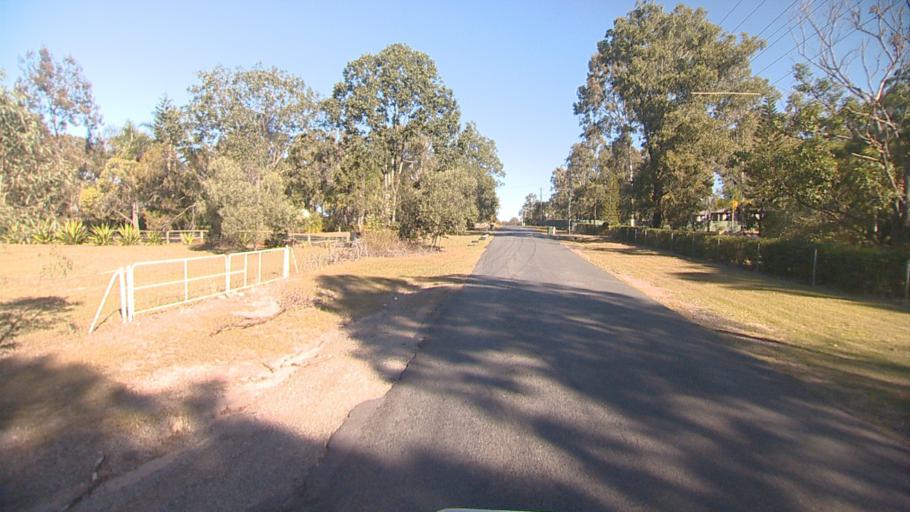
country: AU
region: Queensland
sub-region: Logan
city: Park Ridge South
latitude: -27.7248
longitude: 153.0205
